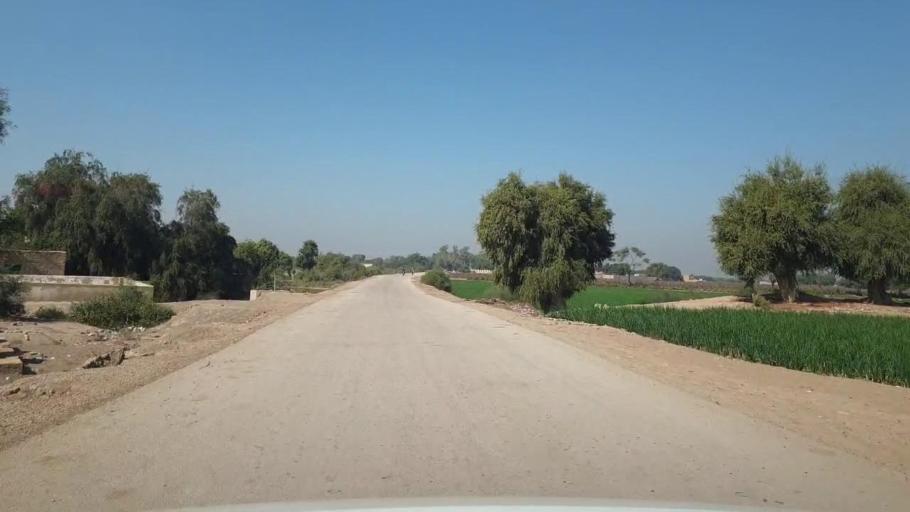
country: PK
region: Sindh
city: Bhan
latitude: 26.6462
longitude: 67.7173
